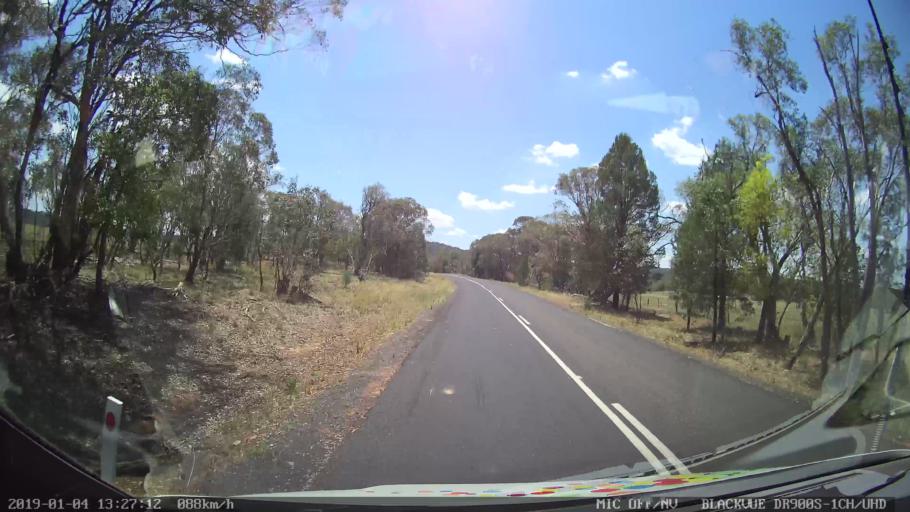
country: AU
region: New South Wales
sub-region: Parkes
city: Peak Hill
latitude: -32.6717
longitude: 148.5612
